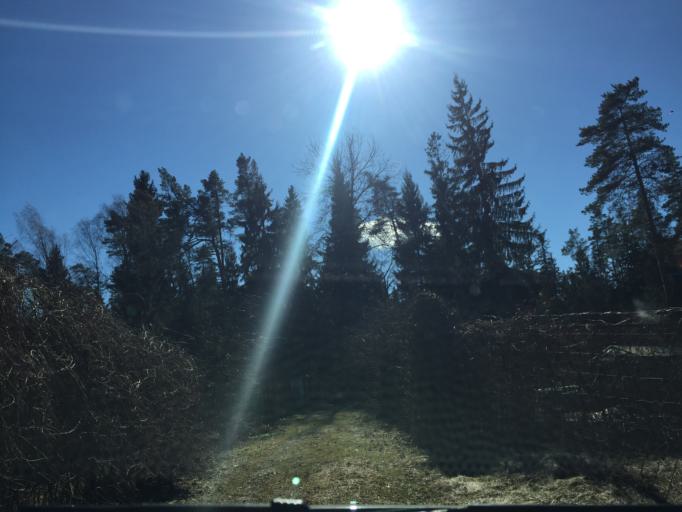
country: LV
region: Incukalns
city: Vangazi
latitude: 57.0908
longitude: 24.5327
